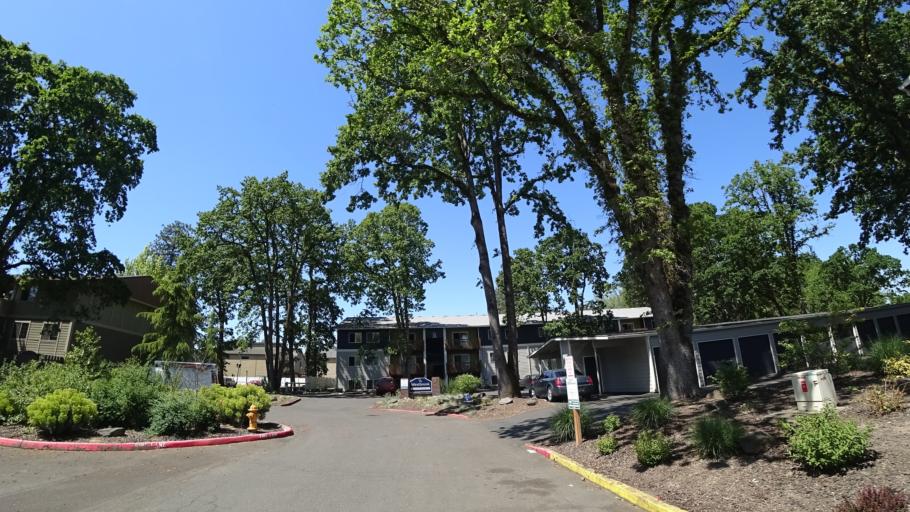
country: US
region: Oregon
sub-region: Washington County
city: Aloha
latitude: 45.4975
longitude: -122.8542
